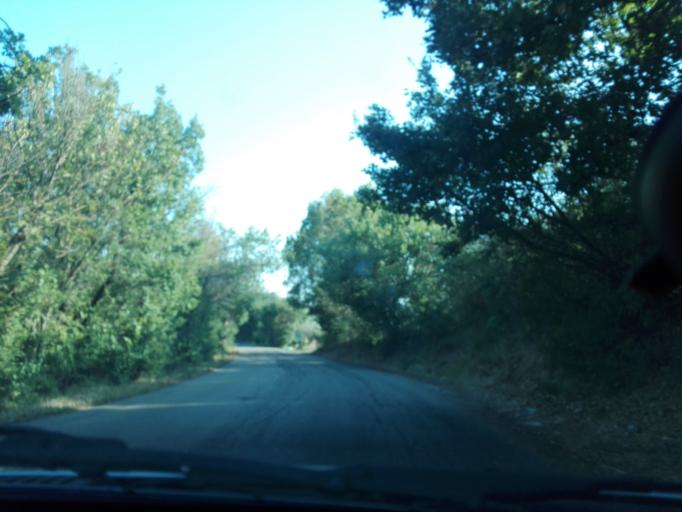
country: IT
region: Abruzzo
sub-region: Provincia di Pescara
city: Cappelle sul Tavo
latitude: 42.4458
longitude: 14.0923
